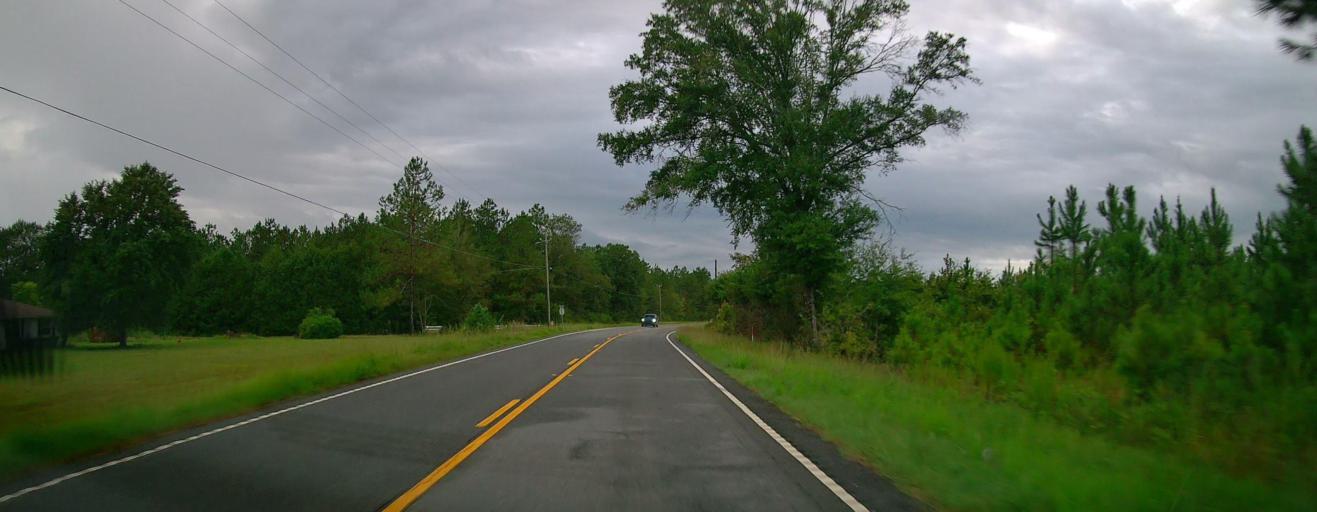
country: US
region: Georgia
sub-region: Ware County
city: Deenwood
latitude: 31.2791
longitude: -82.4240
